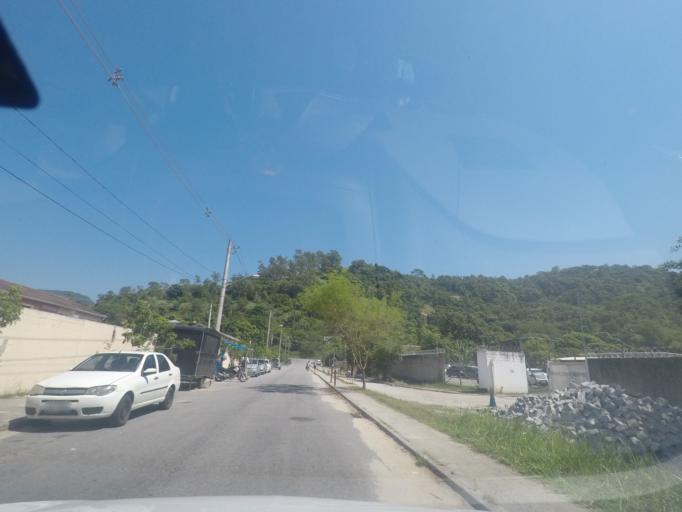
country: BR
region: Rio de Janeiro
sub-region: Nilopolis
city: Nilopolis
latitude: -22.9894
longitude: -43.4850
